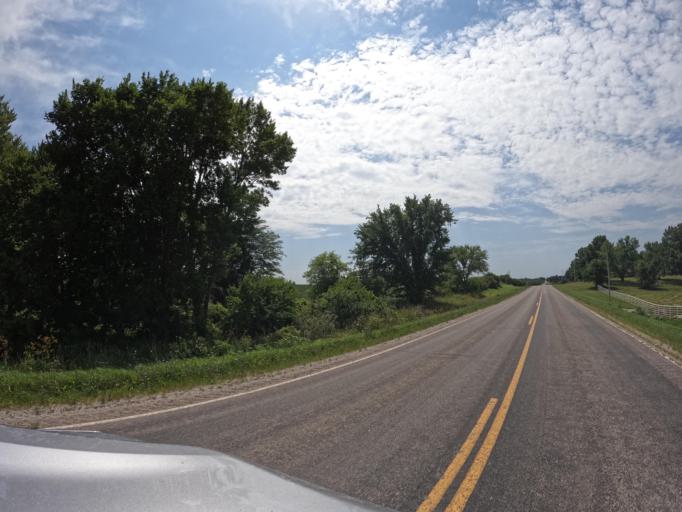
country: US
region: Iowa
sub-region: Appanoose County
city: Centerville
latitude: 40.8039
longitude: -92.9449
